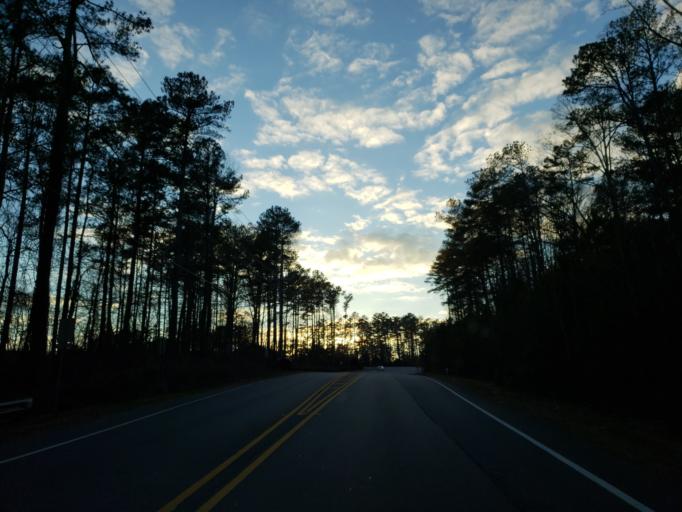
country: US
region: Georgia
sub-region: Cobb County
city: Acworth
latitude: 33.9950
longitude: -84.6948
